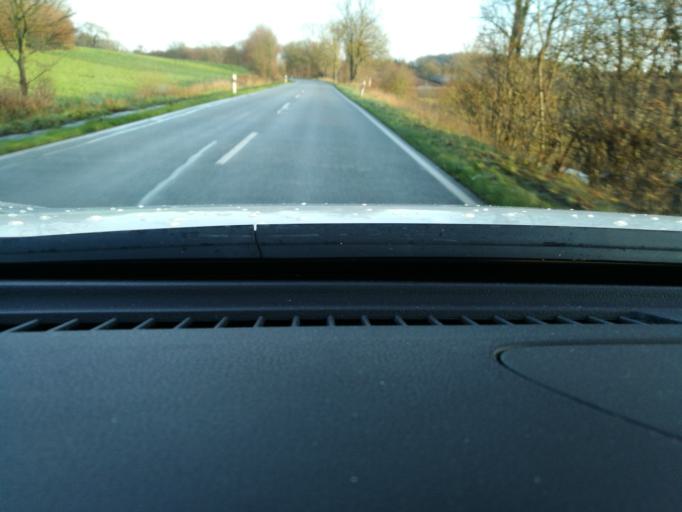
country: DE
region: Schleswig-Holstein
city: Ascheffel
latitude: 54.4136
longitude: 9.7008
